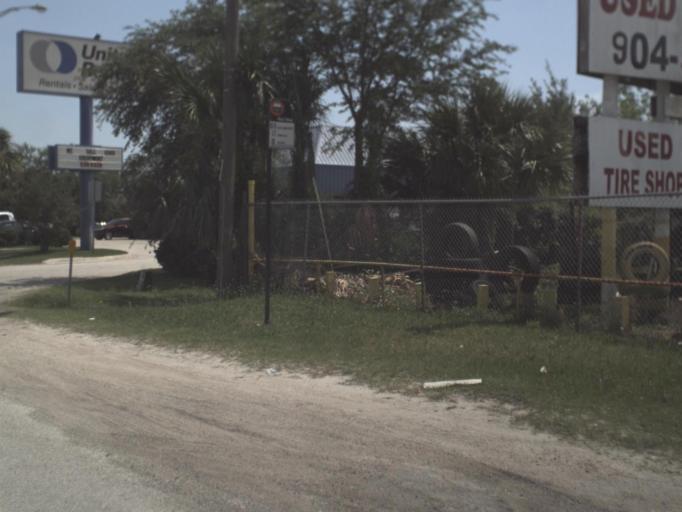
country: US
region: Florida
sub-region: Duval County
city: Jacksonville
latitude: 30.2689
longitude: -81.6205
